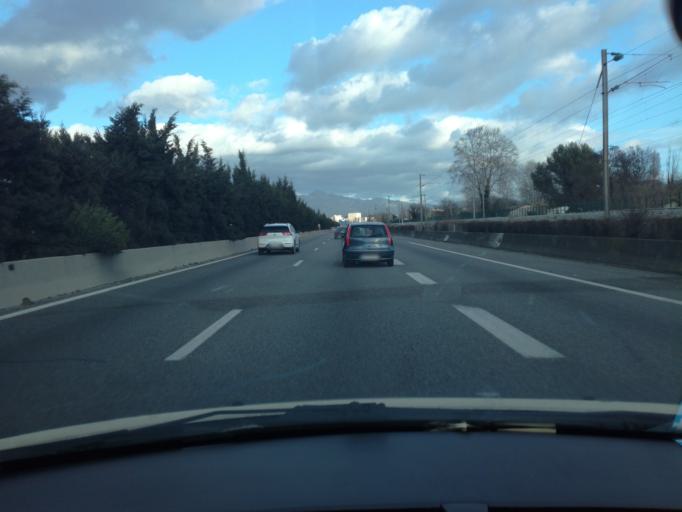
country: FR
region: Provence-Alpes-Cote d'Azur
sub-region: Departement des Bouches-du-Rhone
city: La Penne-sur-Huveaune
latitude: 43.2860
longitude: 5.5343
